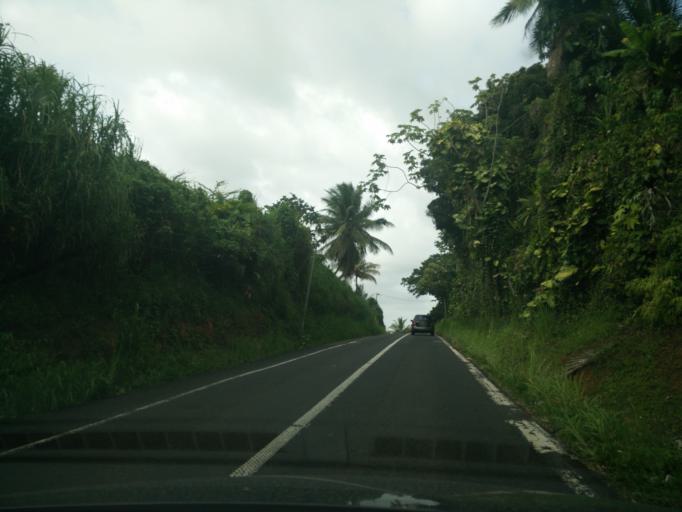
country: GP
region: Guadeloupe
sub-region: Guadeloupe
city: Petit-Bourg
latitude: 16.1933
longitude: -61.6555
